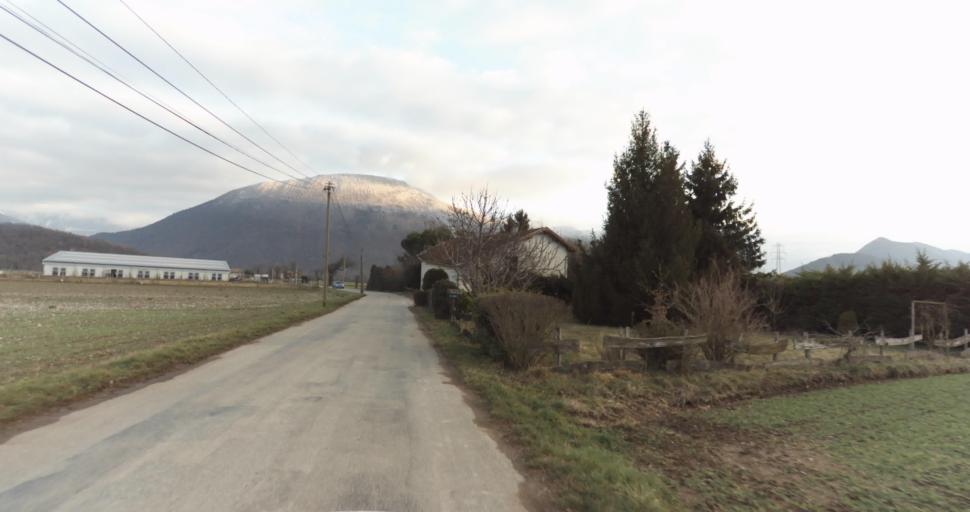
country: FR
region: Rhone-Alpes
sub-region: Departement de l'Isere
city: Allieres-et-Risset
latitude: 45.0801
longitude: 5.6979
